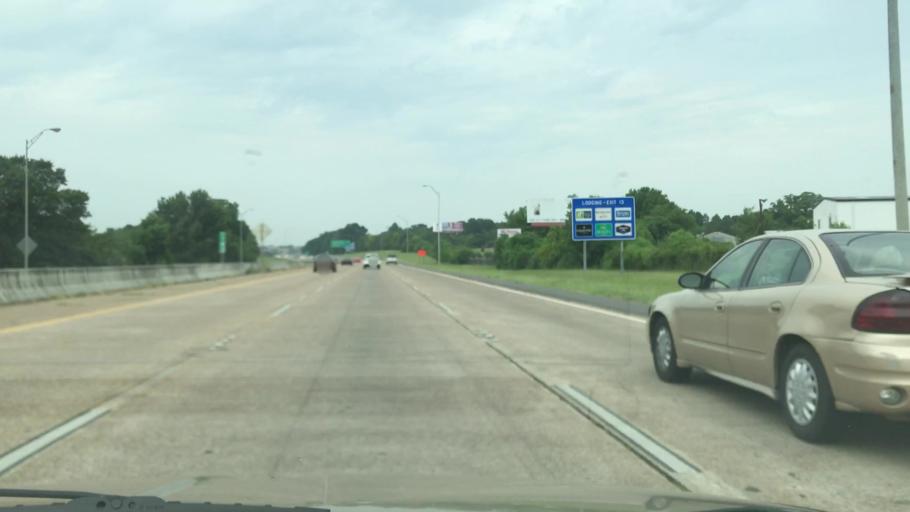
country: US
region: Louisiana
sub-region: Caddo Parish
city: Shreveport
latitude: 32.4685
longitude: -93.8095
